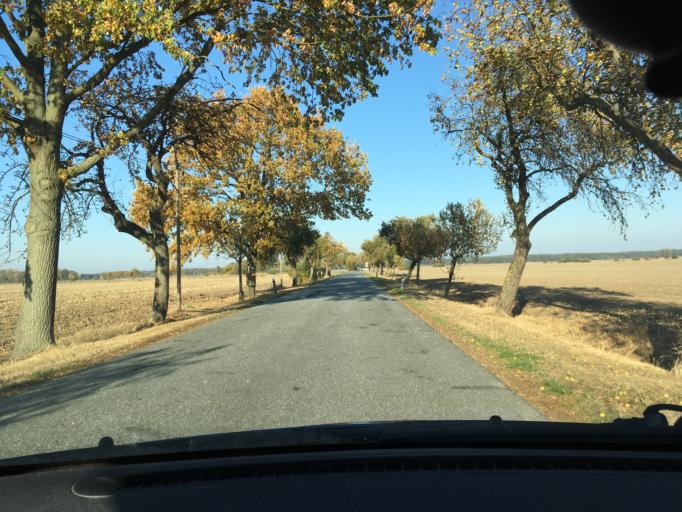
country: DE
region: Lower Saxony
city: Hitzacker
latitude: 53.1730
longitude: 11.0395
